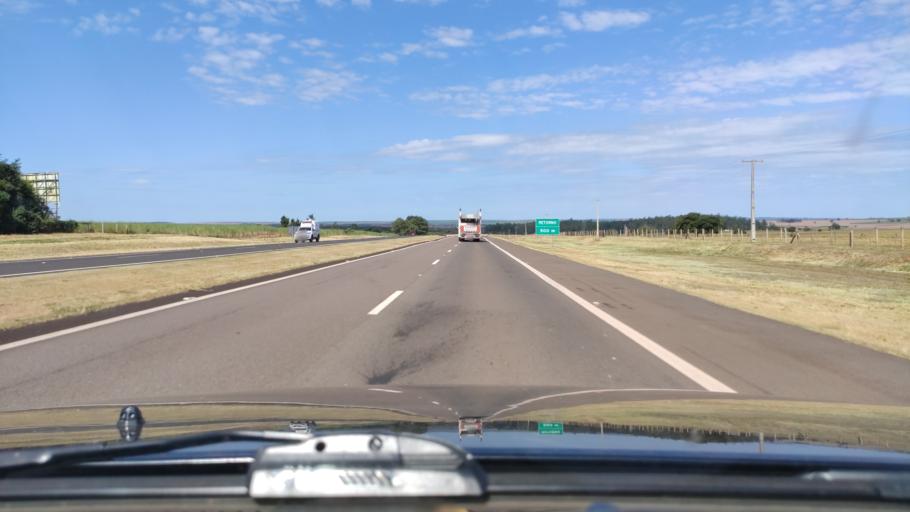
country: BR
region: Sao Paulo
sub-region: Rancharia
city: Rancharia
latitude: -22.4574
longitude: -50.9706
